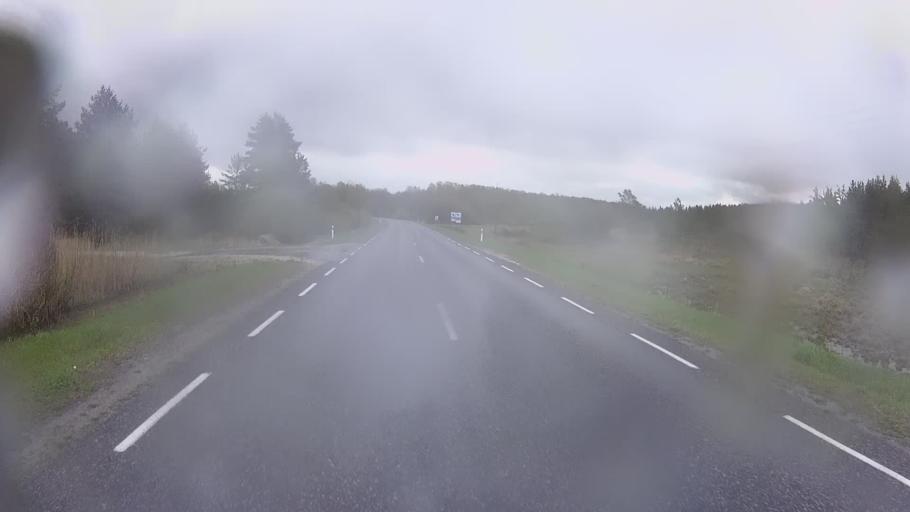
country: EE
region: Hiiumaa
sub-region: Kaerdla linn
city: Kardla
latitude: 58.8330
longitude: 22.8151
